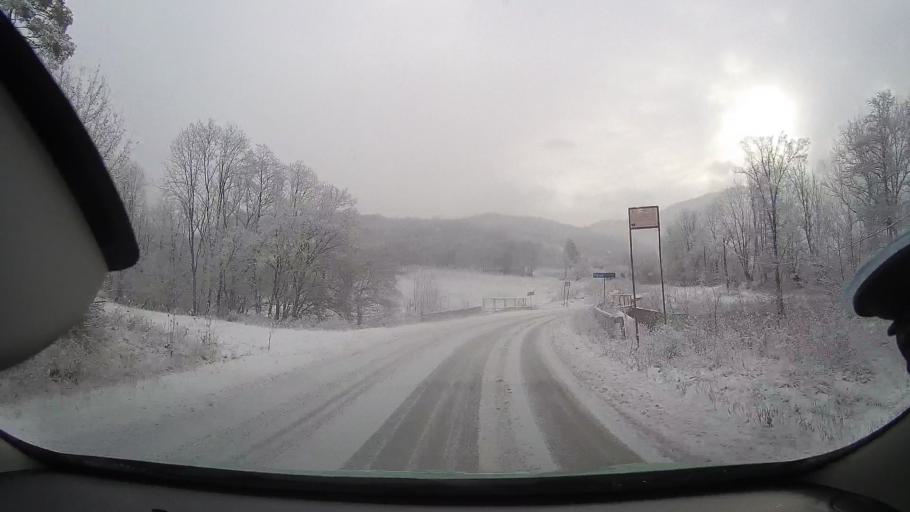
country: RO
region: Alba
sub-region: Comuna Rimetea
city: Rimetea
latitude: 46.4784
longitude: 23.5824
